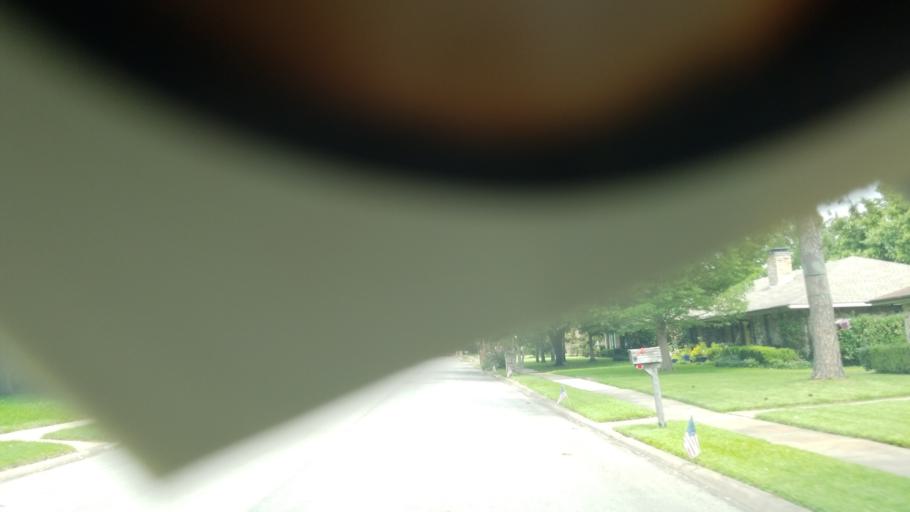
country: US
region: Texas
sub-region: Dallas County
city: Irving
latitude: 32.8499
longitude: -96.9545
